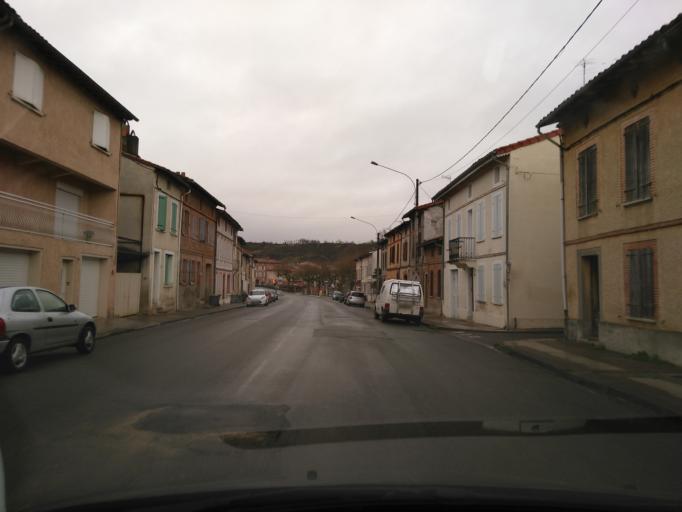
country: FR
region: Midi-Pyrenees
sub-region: Departement de la Haute-Garonne
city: Montesquieu-Volvestre
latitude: 43.2042
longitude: 1.2281
